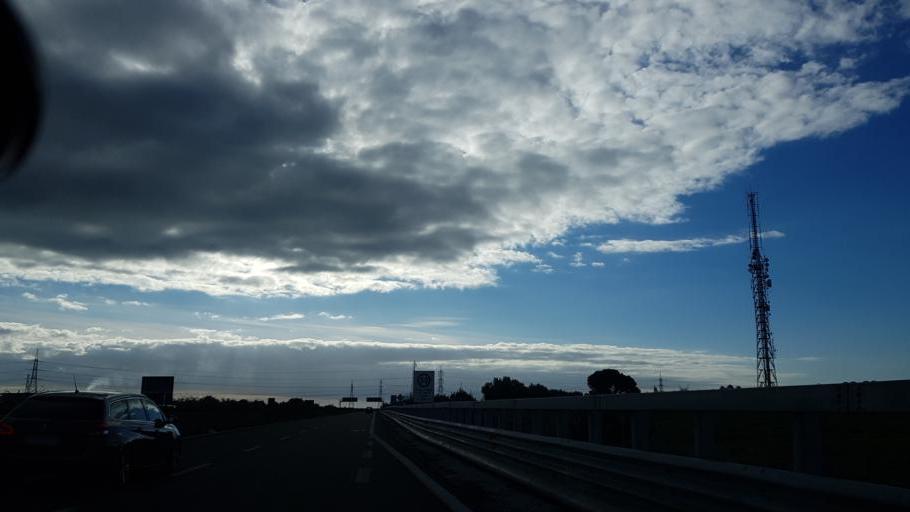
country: IT
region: Apulia
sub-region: Provincia di Brindisi
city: La Rosa
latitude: 40.6124
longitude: 17.9597
